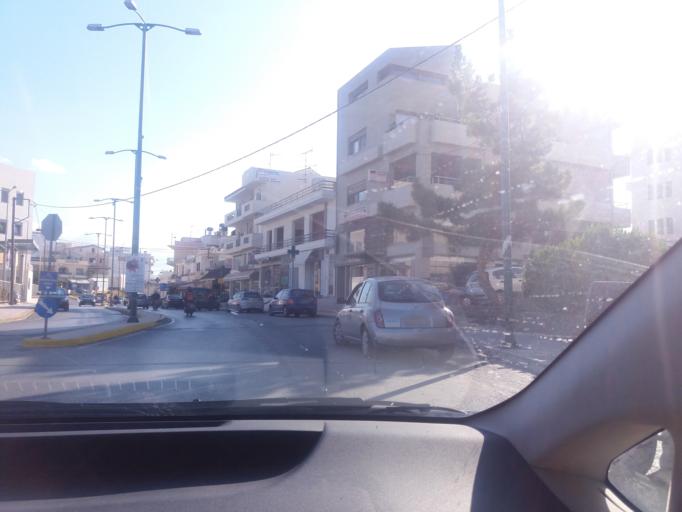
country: GR
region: Crete
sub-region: Nomos Lasithiou
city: Agios Nikolaos
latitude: 35.1951
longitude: 25.7129
